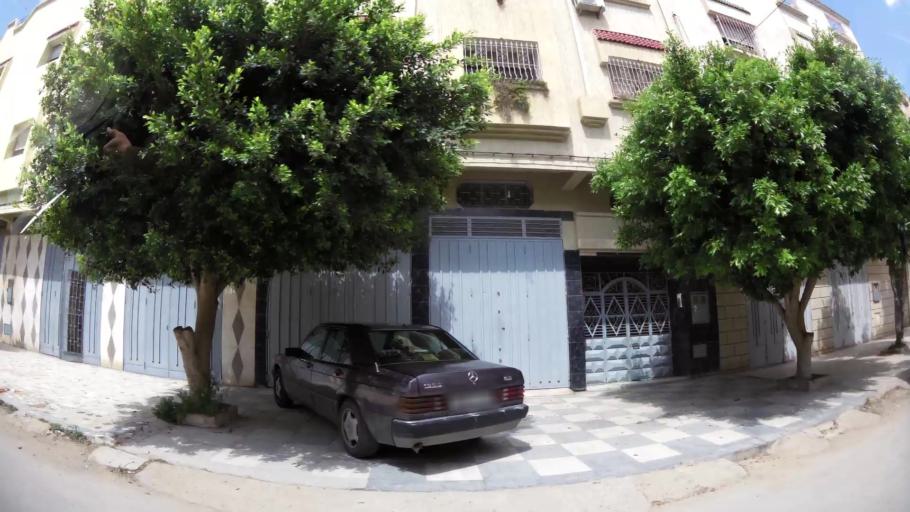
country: MA
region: Oriental
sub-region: Oujda-Angad
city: Oujda
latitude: 34.6839
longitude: -1.9030
